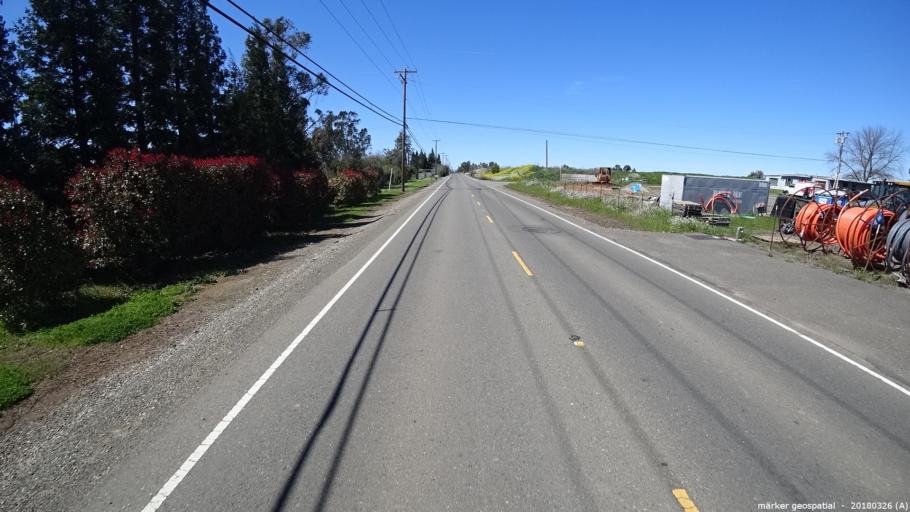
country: US
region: California
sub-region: Sacramento County
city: Vineyard
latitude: 38.4817
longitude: -121.3035
